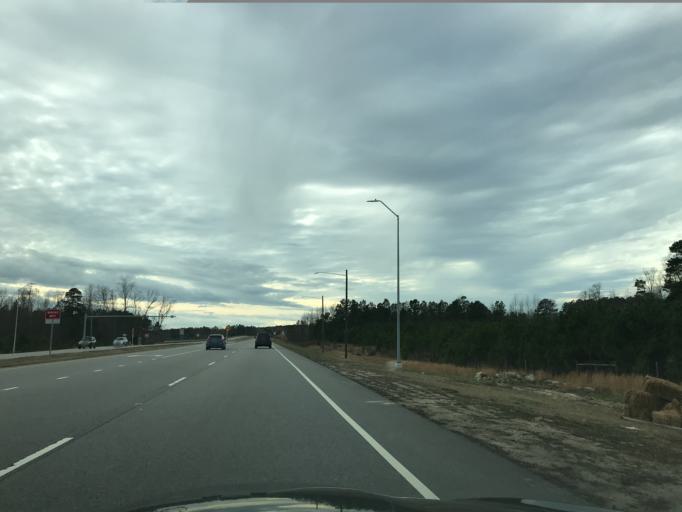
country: US
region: North Carolina
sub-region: Wake County
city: Rolesville
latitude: 35.9129
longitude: -78.4509
